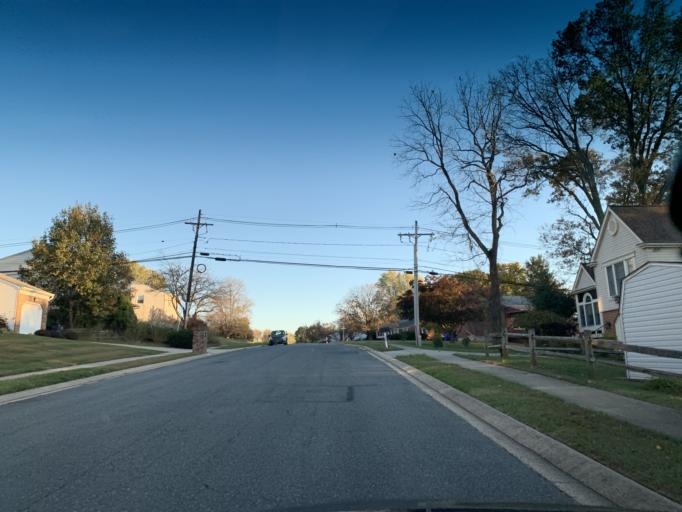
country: US
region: Maryland
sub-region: Harford County
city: Bel Air North
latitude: 39.5599
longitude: -76.3776
